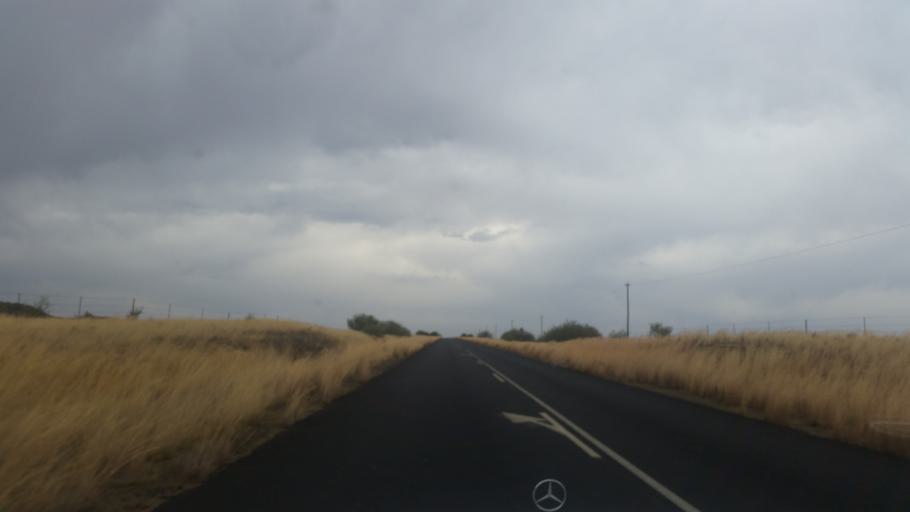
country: ZA
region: Orange Free State
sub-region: Xhariep District Municipality
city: Trompsburg
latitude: -30.4255
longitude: 26.1177
